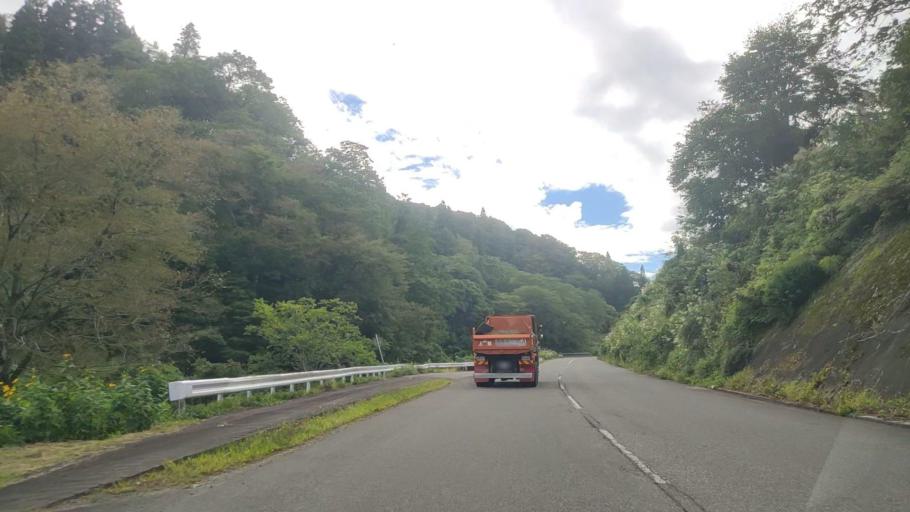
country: JP
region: Nagano
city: Iiyama
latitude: 36.8972
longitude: 138.3203
